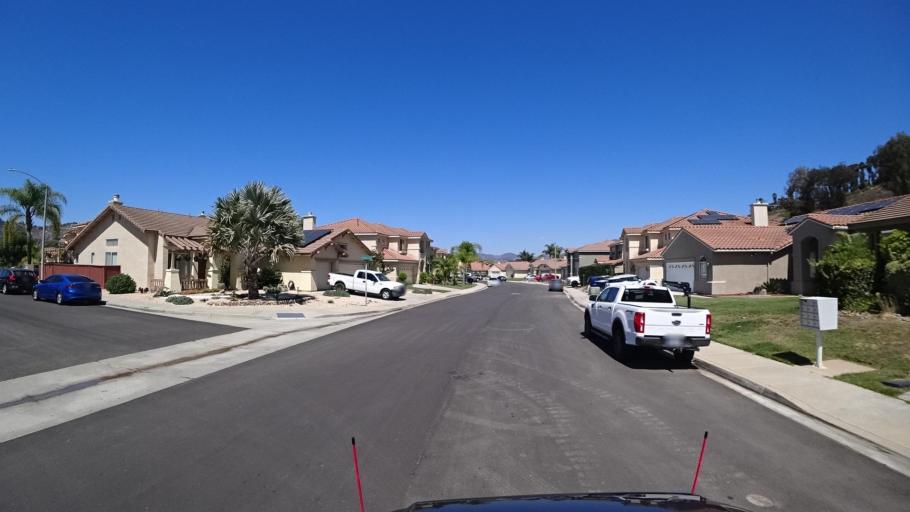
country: US
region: California
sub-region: San Diego County
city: Rainbow
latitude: 33.3288
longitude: -117.1494
